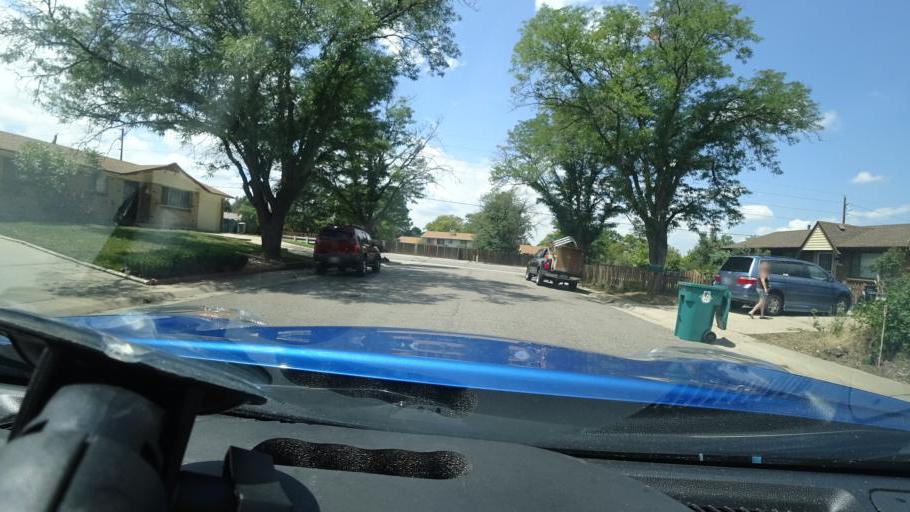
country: US
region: Colorado
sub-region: Adams County
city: Aurora
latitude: 39.7040
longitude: -104.8466
